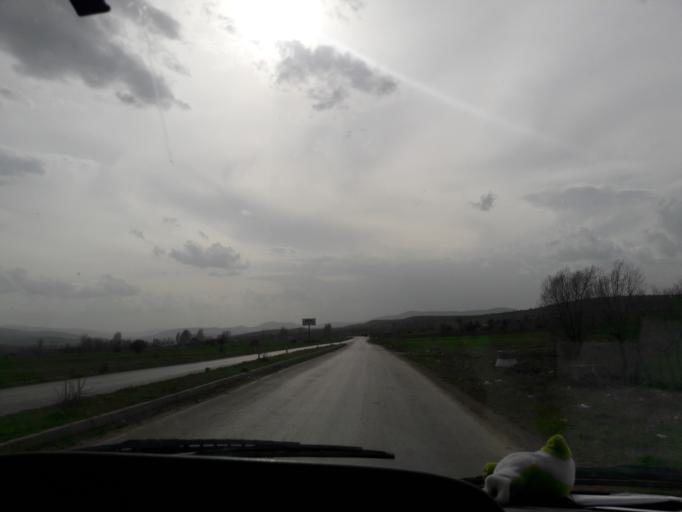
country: TR
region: Gumushane
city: Siran
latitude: 40.1774
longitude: 39.1011
